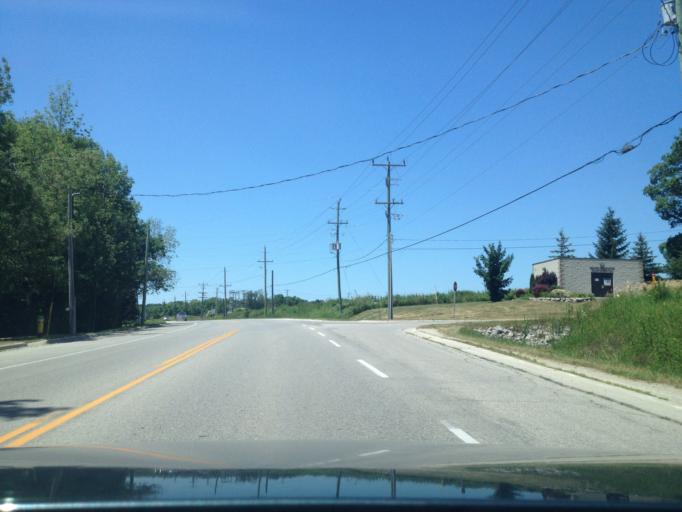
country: CA
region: Ontario
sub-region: Wellington County
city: Guelph
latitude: 43.6924
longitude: -80.4027
